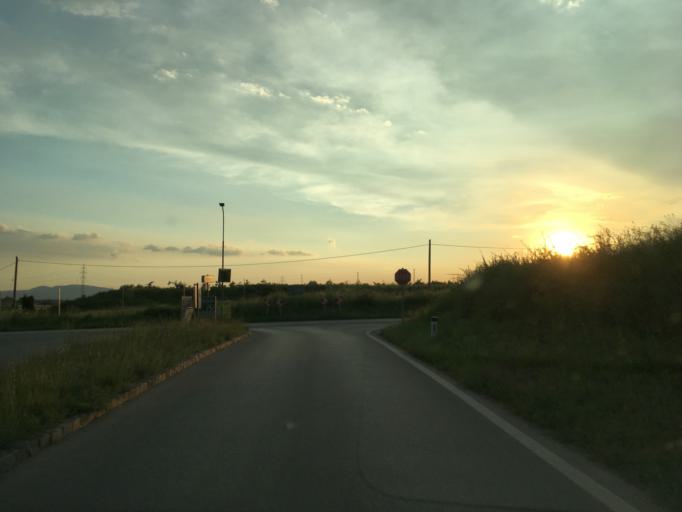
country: AT
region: Lower Austria
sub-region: Politischer Bezirk Wien-Umgebung
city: Gerasdorf bei Wien
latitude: 48.3058
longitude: 16.4856
